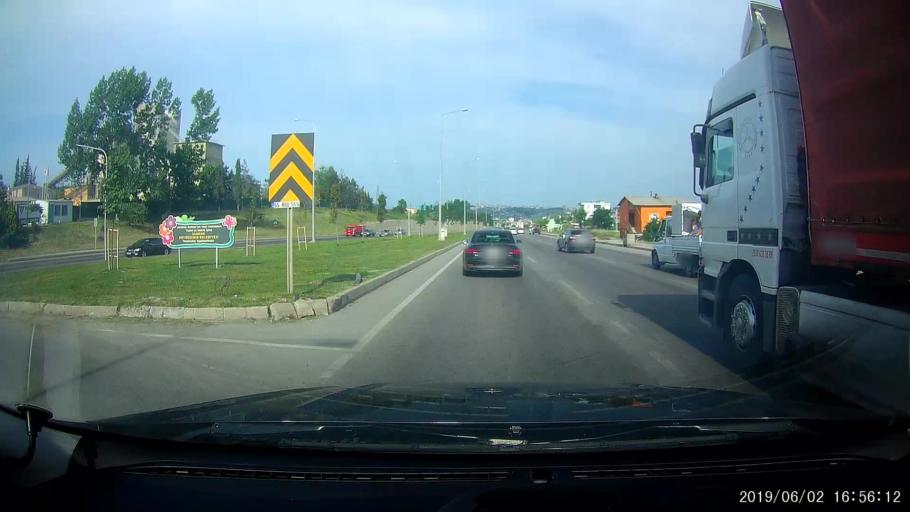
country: TR
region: Samsun
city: Samsun
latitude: 41.2930
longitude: 36.2564
